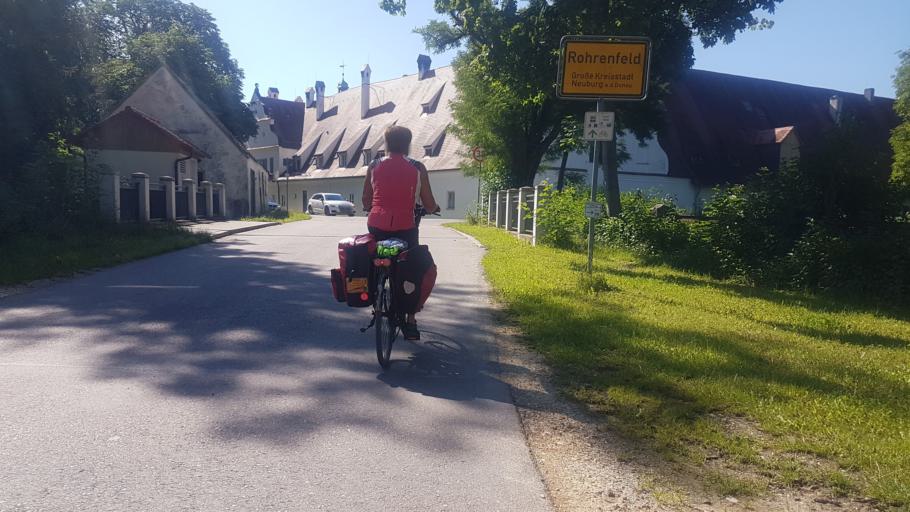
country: DE
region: Bavaria
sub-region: Upper Bavaria
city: Bergheim
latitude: 48.7270
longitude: 11.2731
